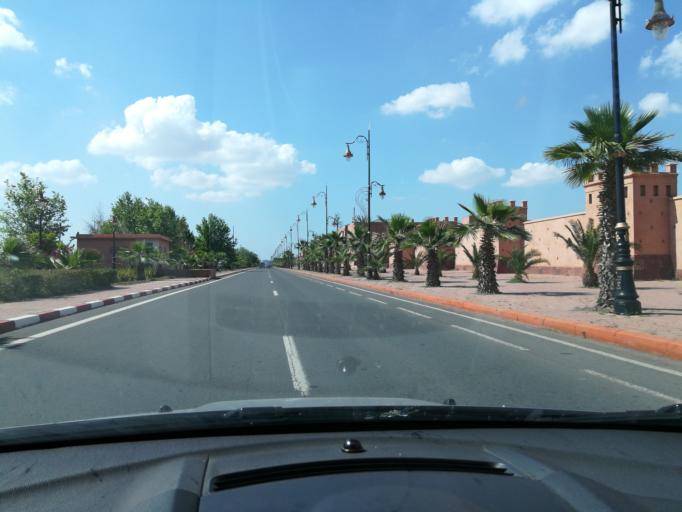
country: MA
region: Marrakech-Tensift-Al Haouz
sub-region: Marrakech
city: Marrakesh
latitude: 31.5894
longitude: -7.9893
